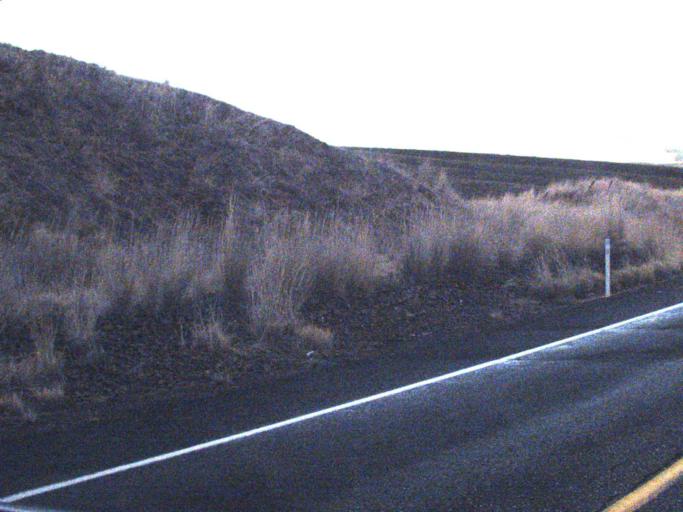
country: US
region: Washington
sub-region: Garfield County
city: Pomeroy
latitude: 46.5808
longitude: -117.7752
